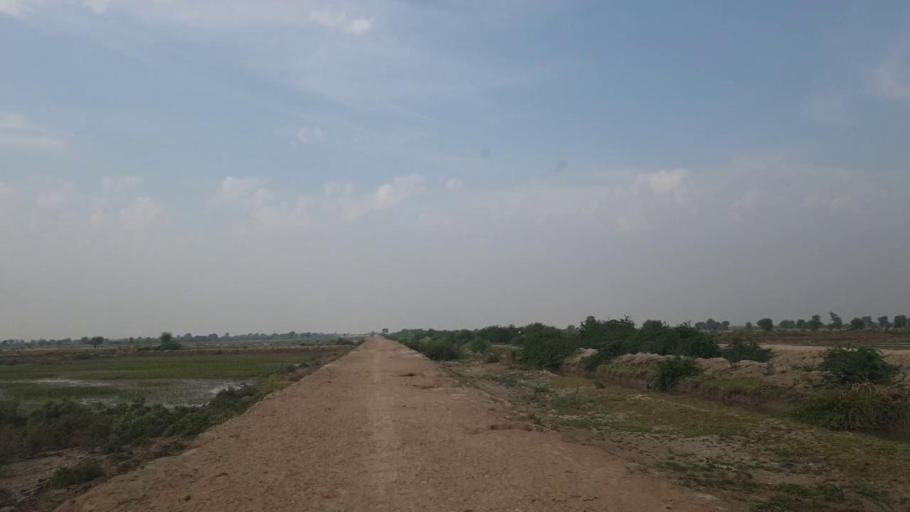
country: PK
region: Sindh
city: Rajo Khanani
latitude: 24.9623
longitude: 69.0192
